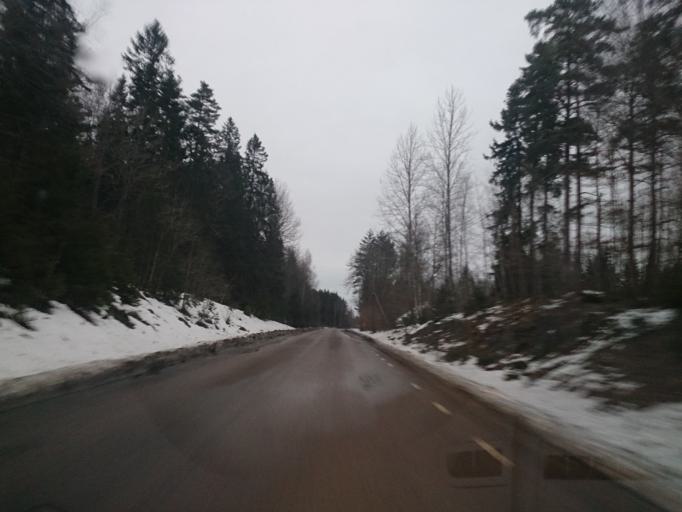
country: SE
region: OEstergoetland
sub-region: Atvidabergs Kommun
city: Atvidaberg
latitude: 58.3192
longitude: 16.0273
